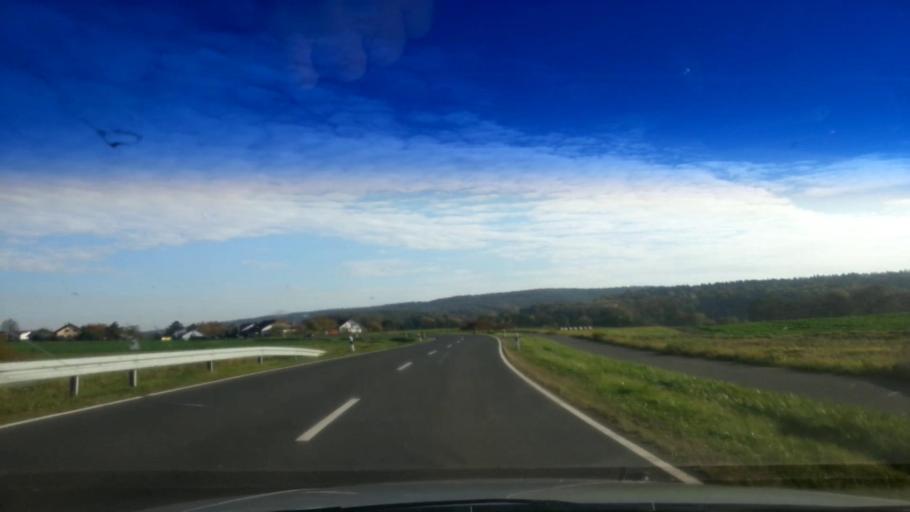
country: DE
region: Bavaria
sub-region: Upper Franconia
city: Stegaurach
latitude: 49.8547
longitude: 10.8714
